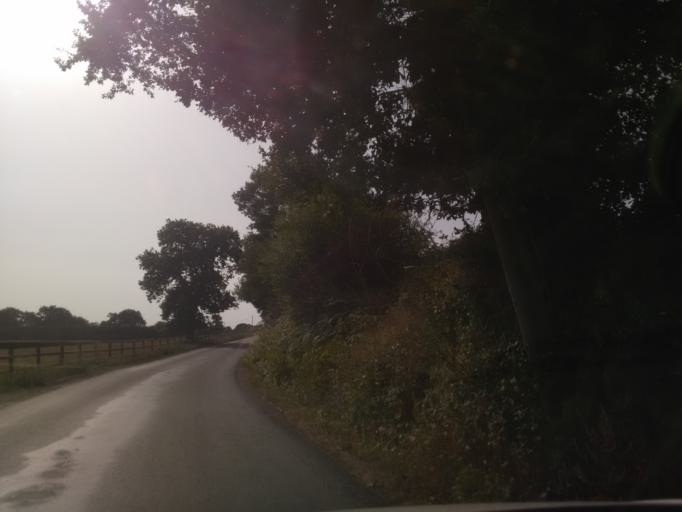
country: FR
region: Brittany
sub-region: Departement d'Ille-et-Vilaine
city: Dinge
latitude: 48.3553
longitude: -1.7337
